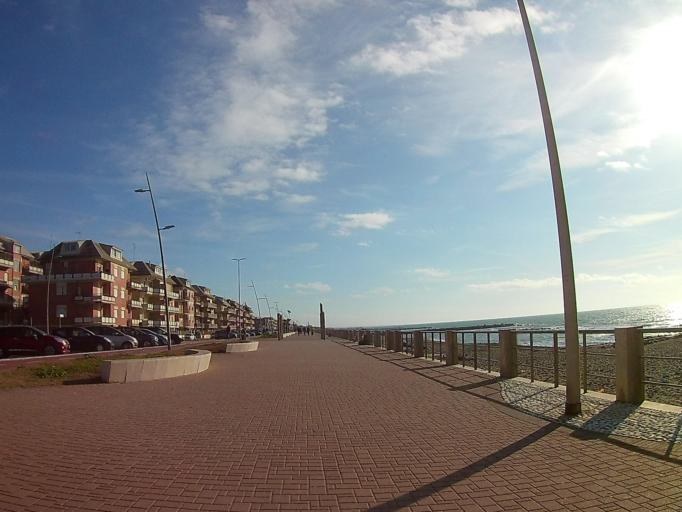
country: IT
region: Latium
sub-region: Citta metropolitana di Roma Capitale
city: Lido di Ostia
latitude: 41.7355
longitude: 12.2570
